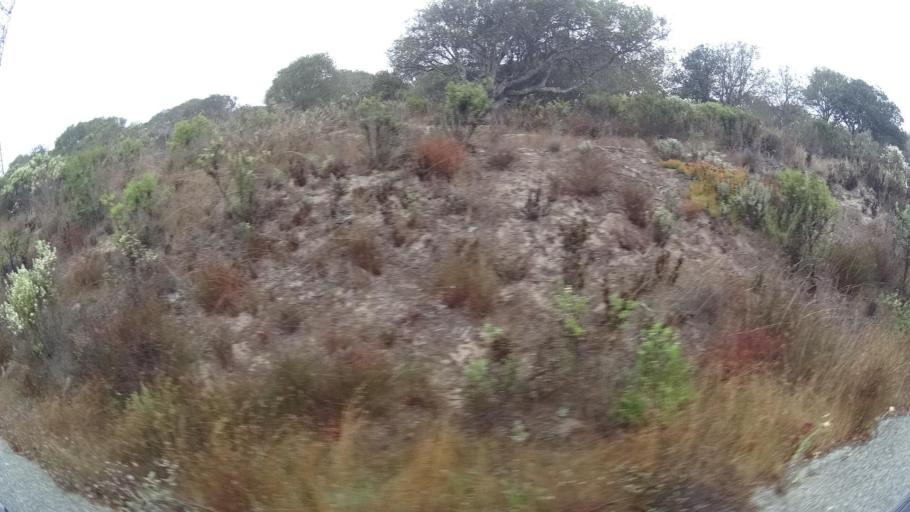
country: US
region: California
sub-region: Monterey County
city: Marina
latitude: 36.6438
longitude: -121.7752
